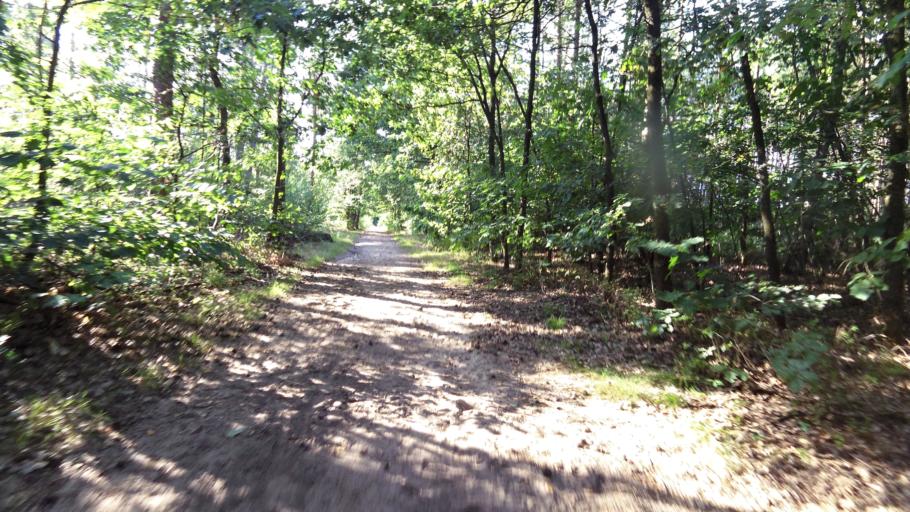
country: NL
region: Gelderland
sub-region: Gemeente Renkum
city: Renkum
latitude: 52.0024
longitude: 5.7241
